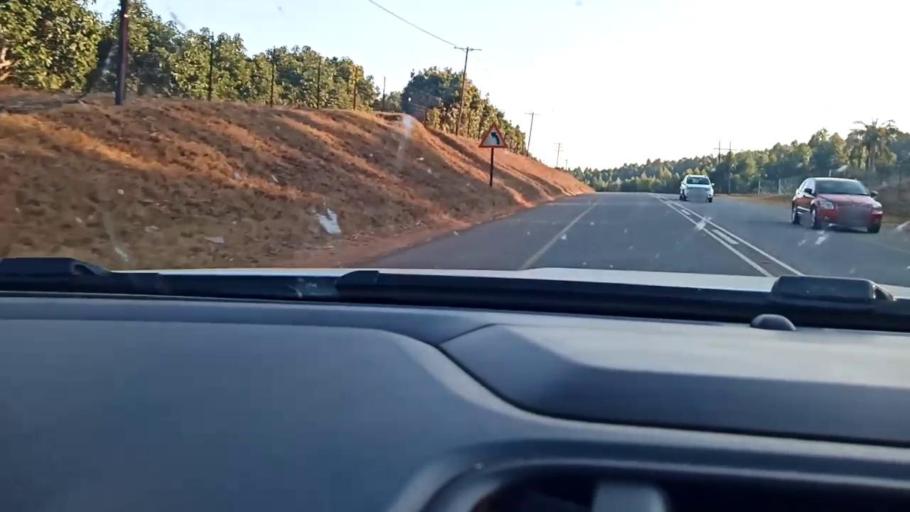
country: ZA
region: Limpopo
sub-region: Mopani District Municipality
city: Duiwelskloof
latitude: -23.7134
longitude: 30.1284
